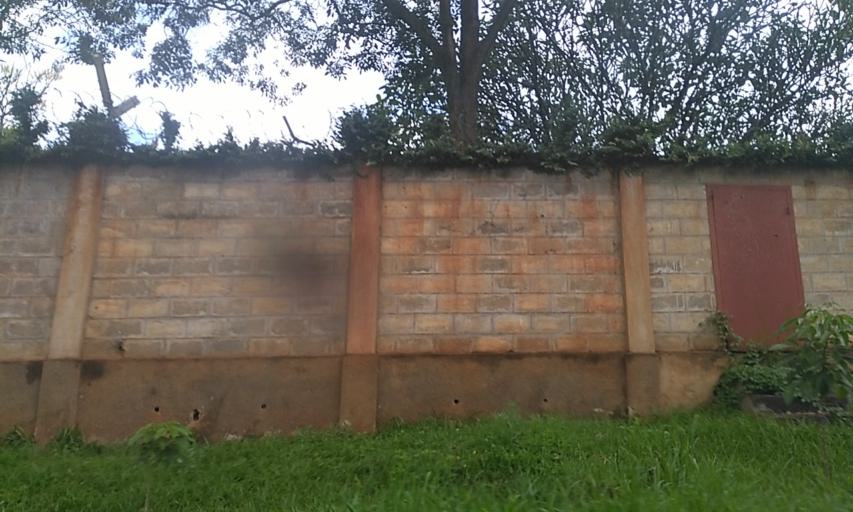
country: UG
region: Central Region
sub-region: Kampala District
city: Kampala
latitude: 0.3280
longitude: 32.5891
